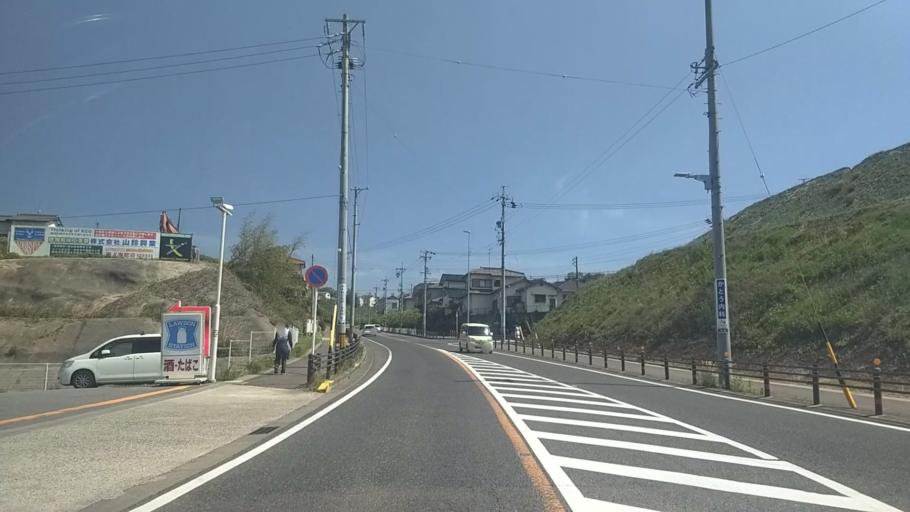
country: JP
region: Aichi
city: Okazaki
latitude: 34.9832
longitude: 137.1969
